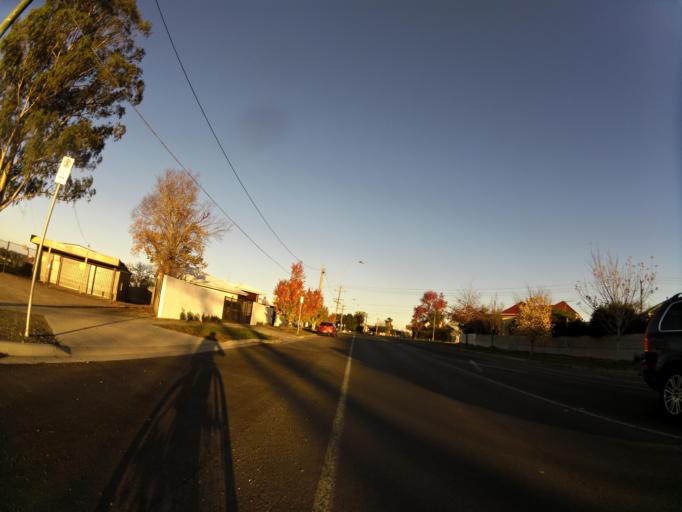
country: AU
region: Victoria
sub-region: Ballarat North
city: Lake Wendouree
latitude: -37.5430
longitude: 143.8438
